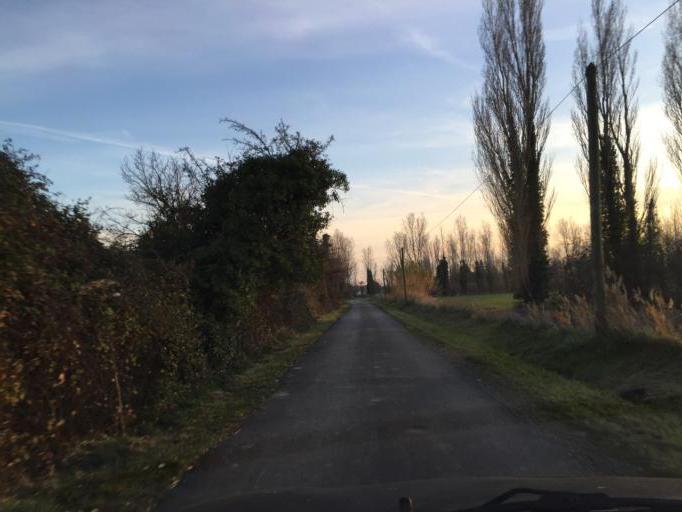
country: FR
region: Provence-Alpes-Cote d'Azur
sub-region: Departement du Vaucluse
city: Camaret-sur-Aigues
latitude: 44.1254
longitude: 4.8565
